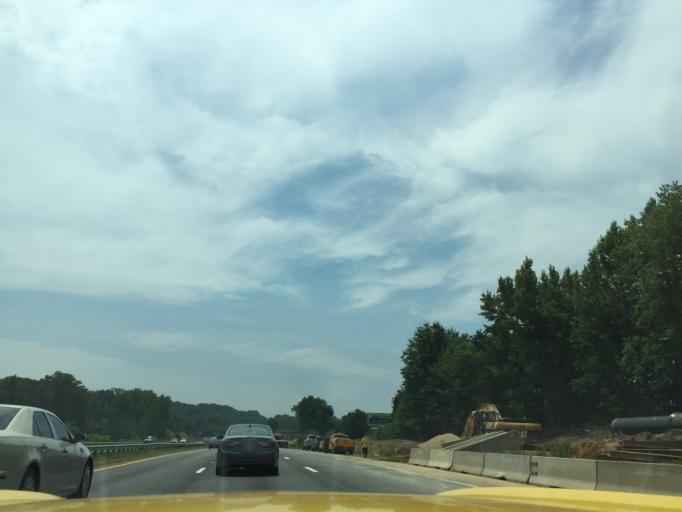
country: US
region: Maryland
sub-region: Prince George's County
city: Friendly
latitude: 38.7322
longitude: -76.9908
